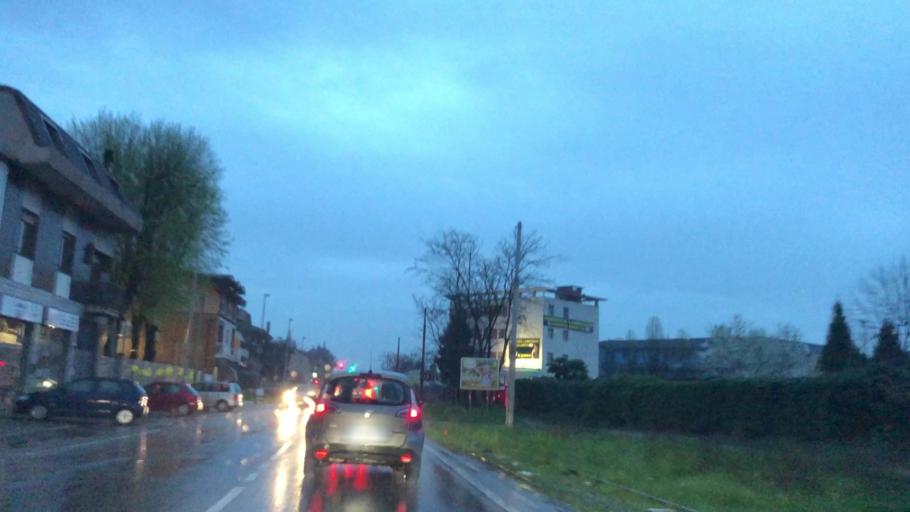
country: IT
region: Lombardy
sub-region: Citta metropolitana di Milano
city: Cusano Milanino
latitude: 45.5683
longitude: 9.1900
